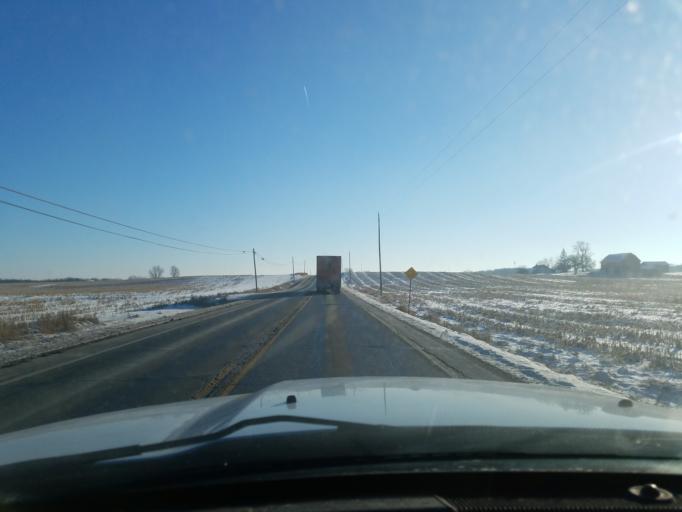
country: US
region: Indiana
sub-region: Noble County
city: Kendallville
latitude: 41.4525
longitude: -85.3253
